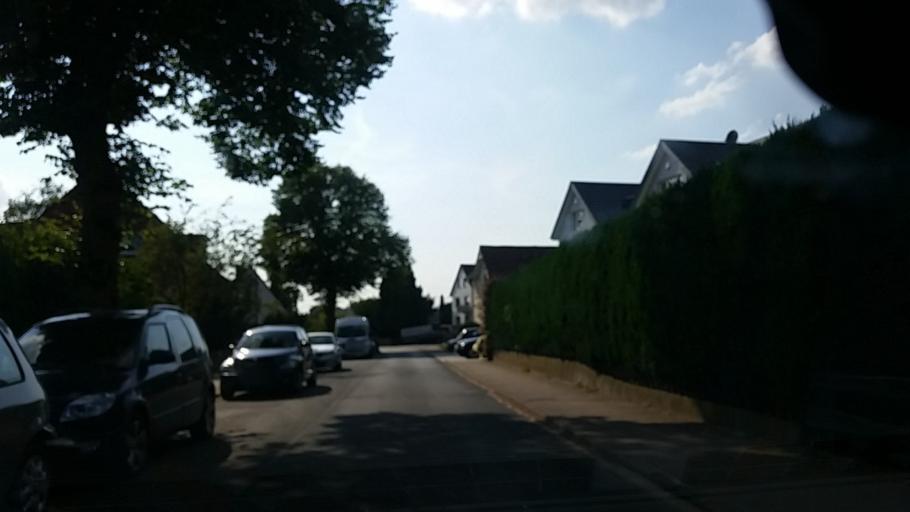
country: DE
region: Schleswig-Holstein
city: Oststeinbek
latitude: 53.5227
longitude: 10.1716
